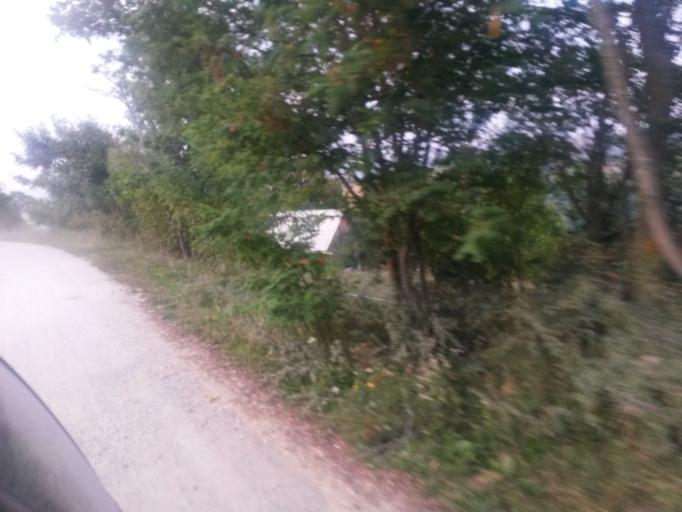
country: RO
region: Alba
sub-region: Comuna Ponor
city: Ponor
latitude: 46.3189
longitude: 23.4161
